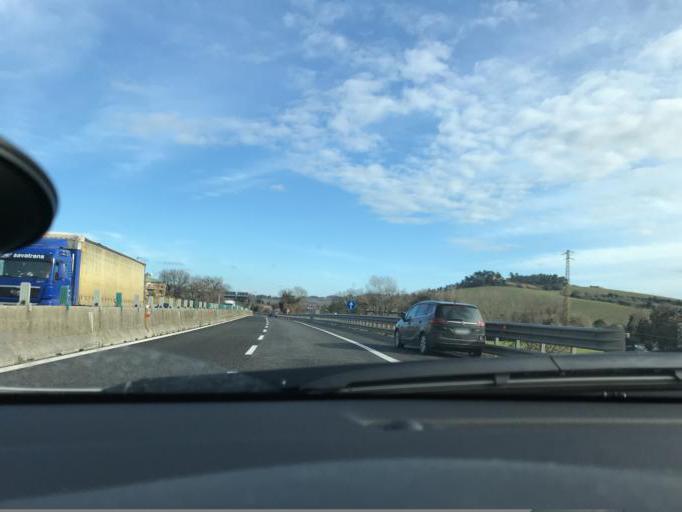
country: IT
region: The Marches
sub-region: Provincia di Ancona
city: Falconara Marittima
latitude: 43.5993
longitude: 13.3594
